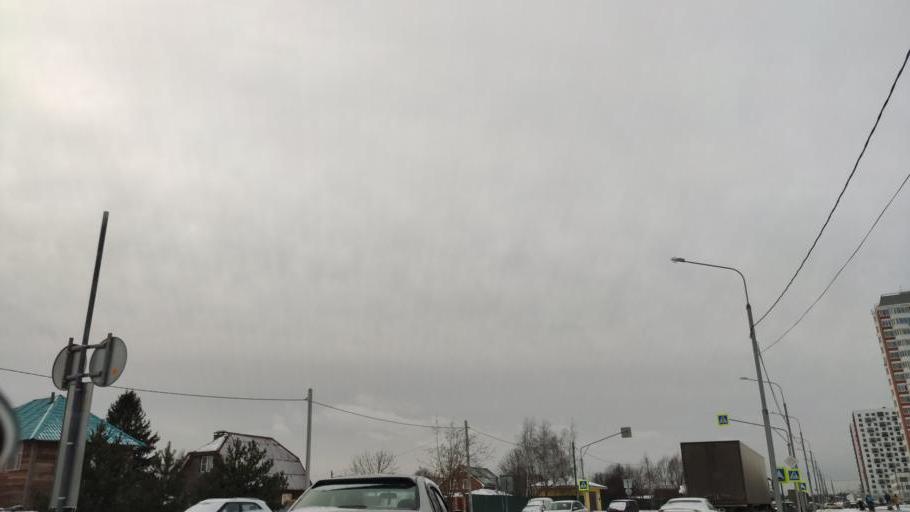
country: RU
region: Moscow
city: Annino
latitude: 55.5273
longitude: 37.6213
